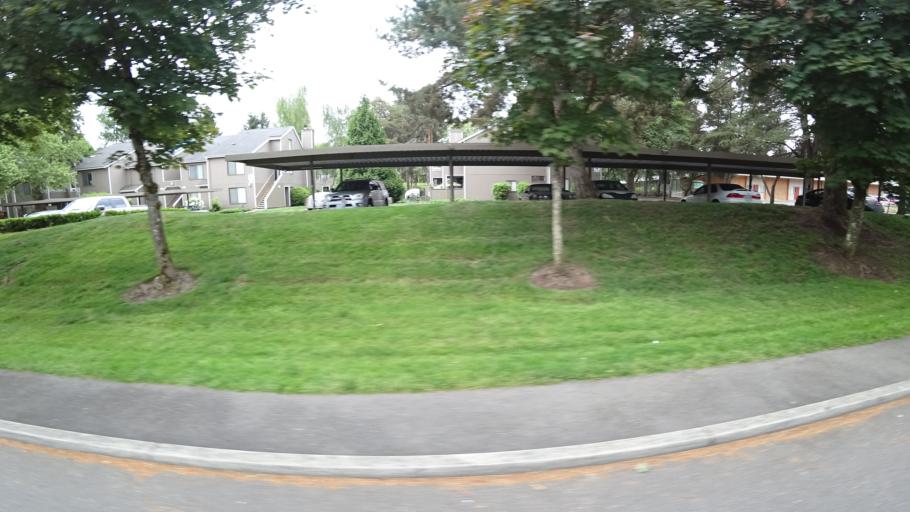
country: US
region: Oregon
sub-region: Washington County
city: Raleigh Hills
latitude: 45.4765
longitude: -122.7506
